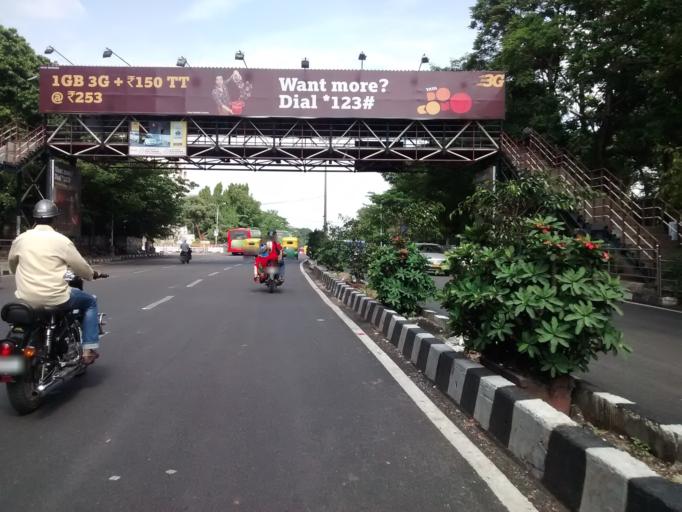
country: IN
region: Karnataka
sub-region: Bangalore Urban
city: Bangalore
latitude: 12.9785
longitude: 77.5836
